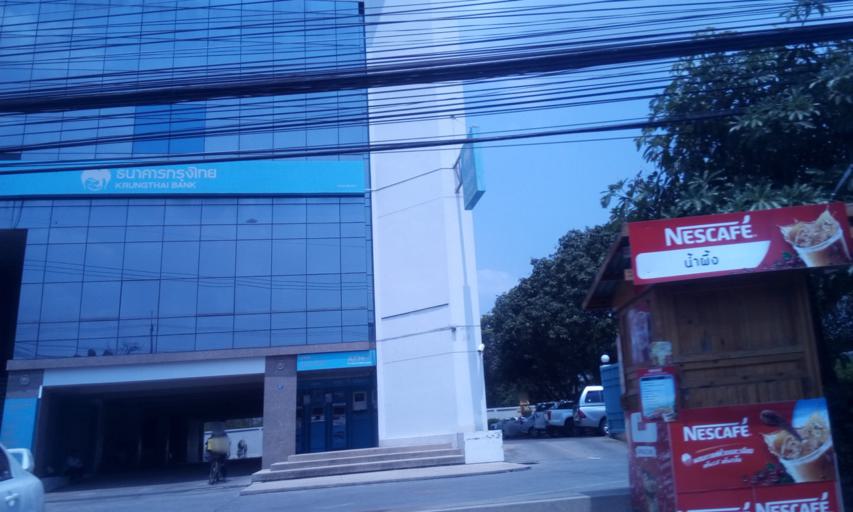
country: TH
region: Chachoengsao
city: Chachoengsao
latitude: 13.6674
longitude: 101.0900
